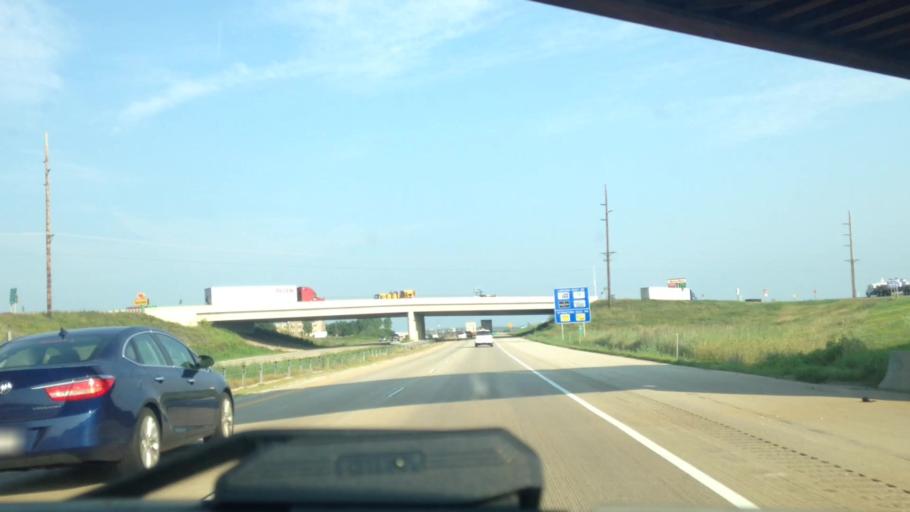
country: US
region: Wisconsin
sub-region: Fond du Lac County
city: Fond du Lac
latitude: 43.7491
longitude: -88.4603
